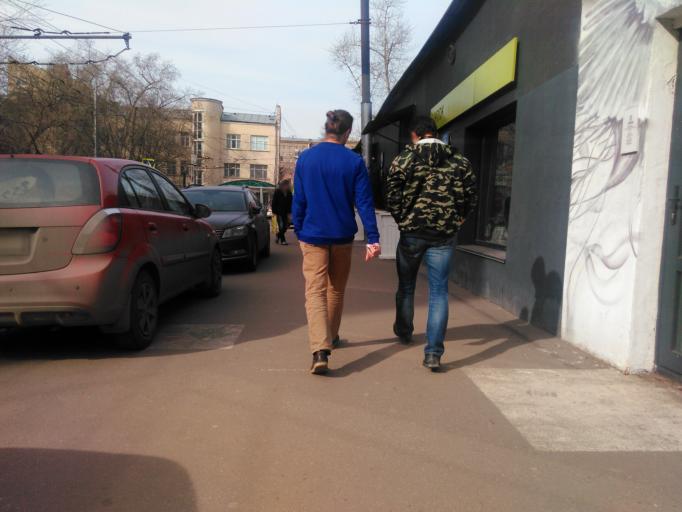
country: RU
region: Moscow
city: Mar'ina Roshcha
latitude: 55.8055
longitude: 37.5844
